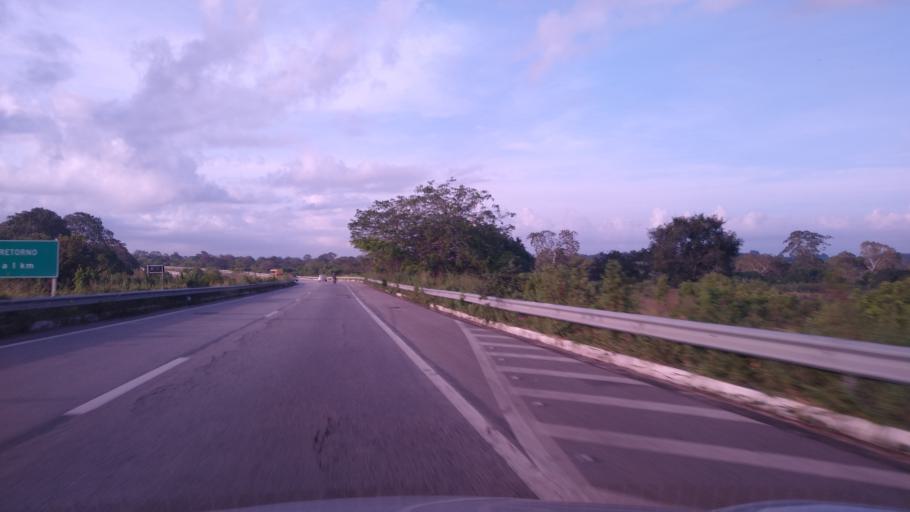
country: BR
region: Ceara
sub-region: Pacajus
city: Pacajus
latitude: -4.1789
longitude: -38.4921
